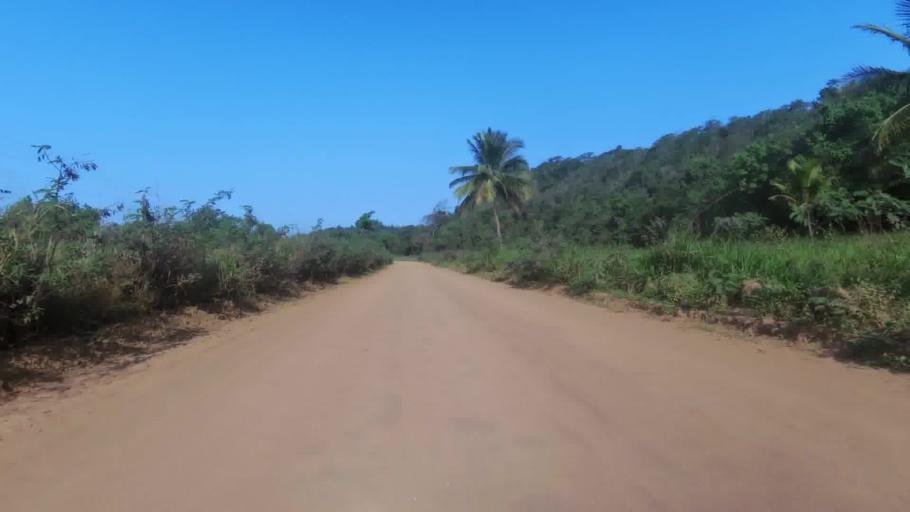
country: BR
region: Espirito Santo
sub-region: Piuma
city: Piuma
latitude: -20.8519
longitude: -40.7620
